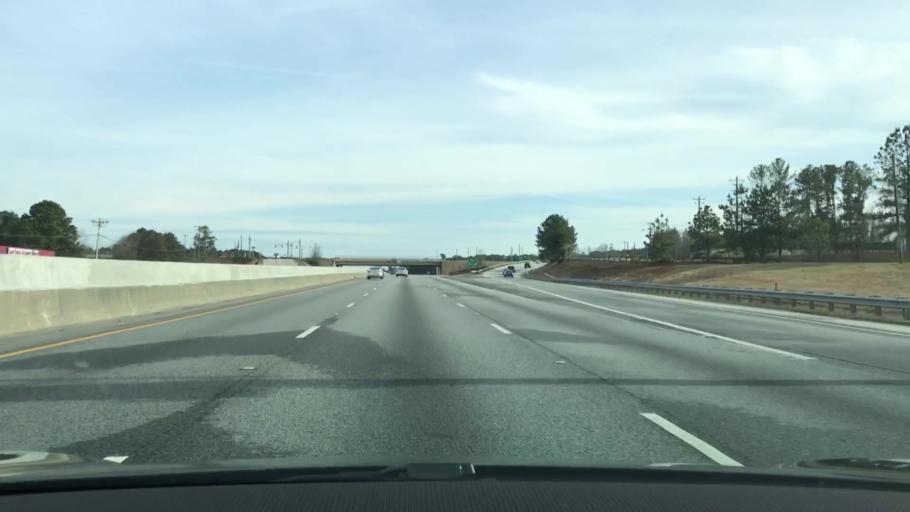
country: US
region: Georgia
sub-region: Rockdale County
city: Conyers
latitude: 33.6379
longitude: -83.9815
